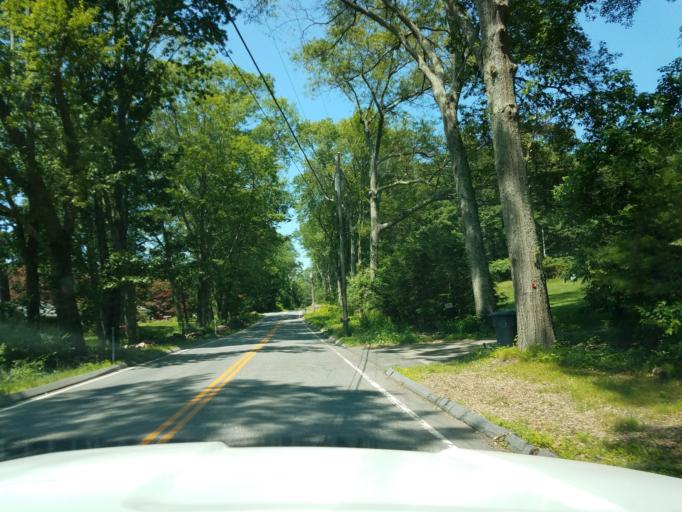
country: US
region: Connecticut
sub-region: Windham County
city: Killingly Center
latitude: 41.8851
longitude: -71.8684
